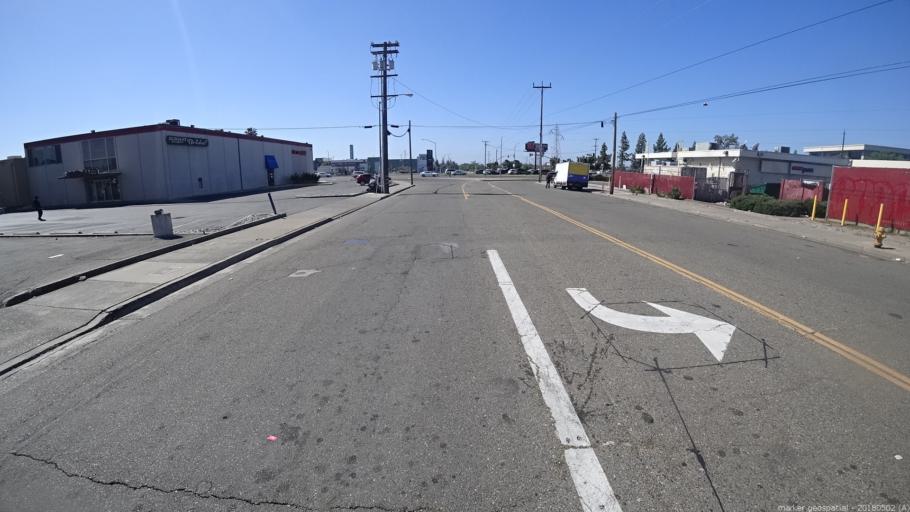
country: US
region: California
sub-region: Sacramento County
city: Arden-Arcade
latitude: 38.5971
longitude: -121.4199
